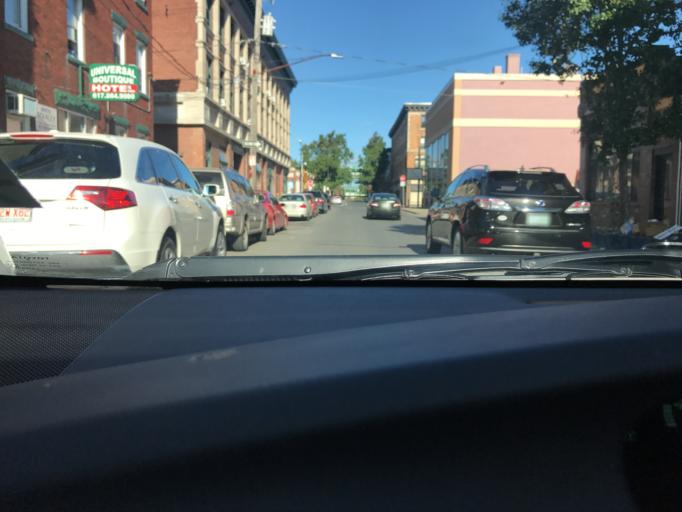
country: US
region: Massachusetts
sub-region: Suffolk County
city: Chelsea
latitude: 42.3903
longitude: -71.0370
